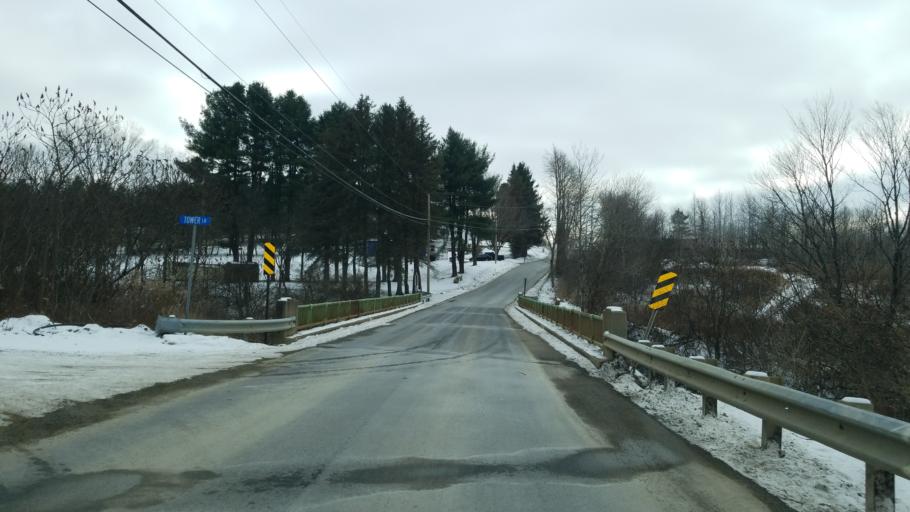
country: US
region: Pennsylvania
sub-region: Clearfield County
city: Sandy
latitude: 41.0806
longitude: -78.7503
